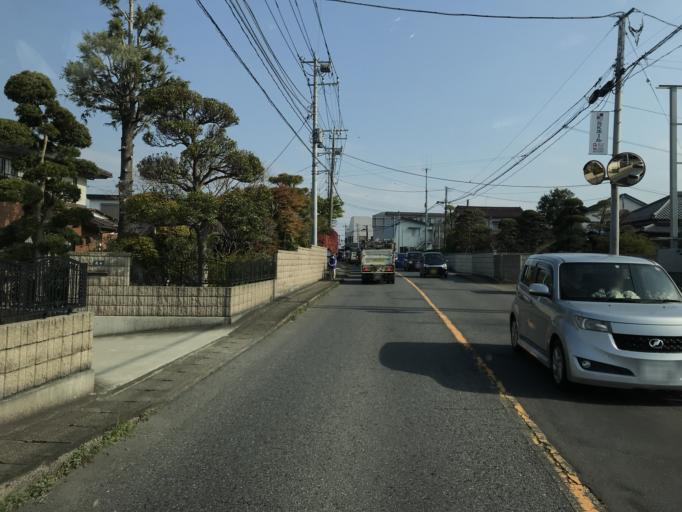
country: JP
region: Chiba
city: Narita
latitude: 35.7586
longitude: 140.3046
